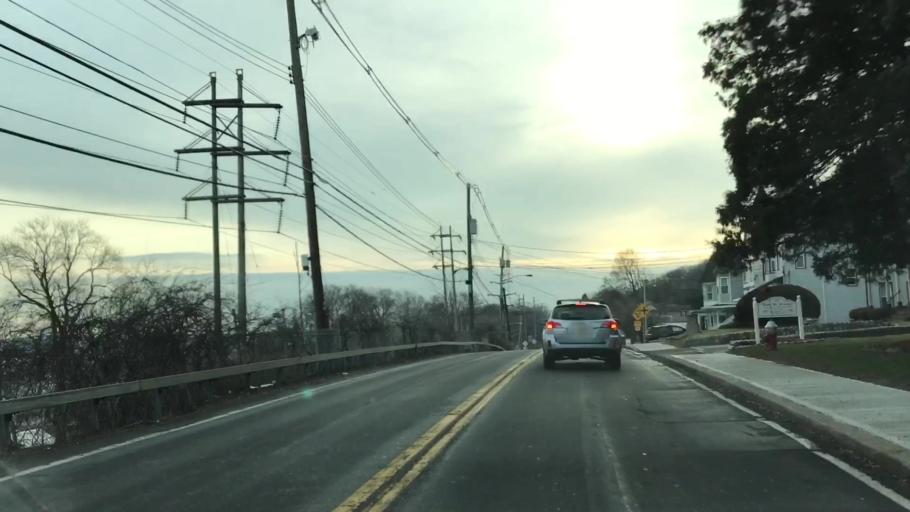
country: US
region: New York
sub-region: Rockland County
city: Haverstraw
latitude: 41.1957
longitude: -73.9708
